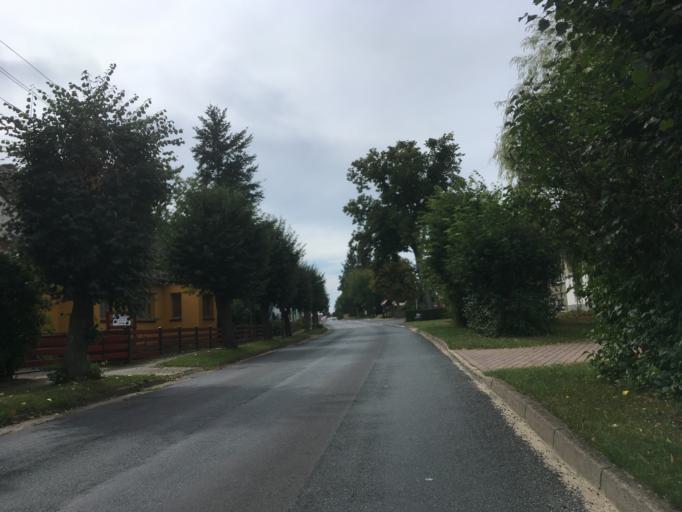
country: DE
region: Brandenburg
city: Mittenwalde
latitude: 53.2449
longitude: 13.6415
